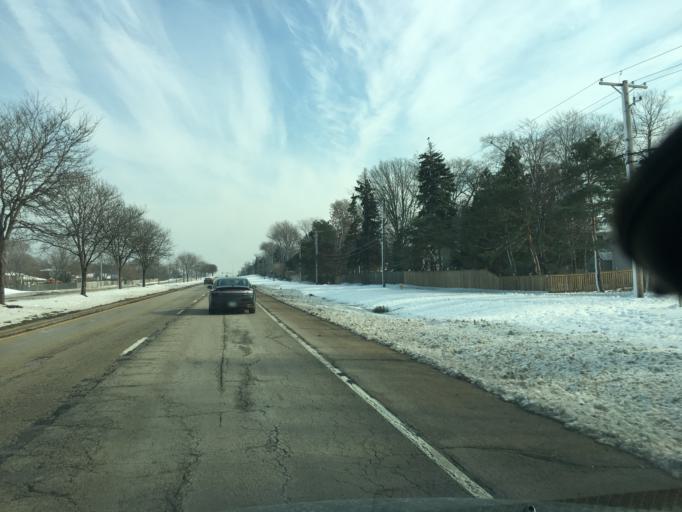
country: US
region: Illinois
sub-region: DuPage County
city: Darien
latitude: 41.7514
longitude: -87.9906
